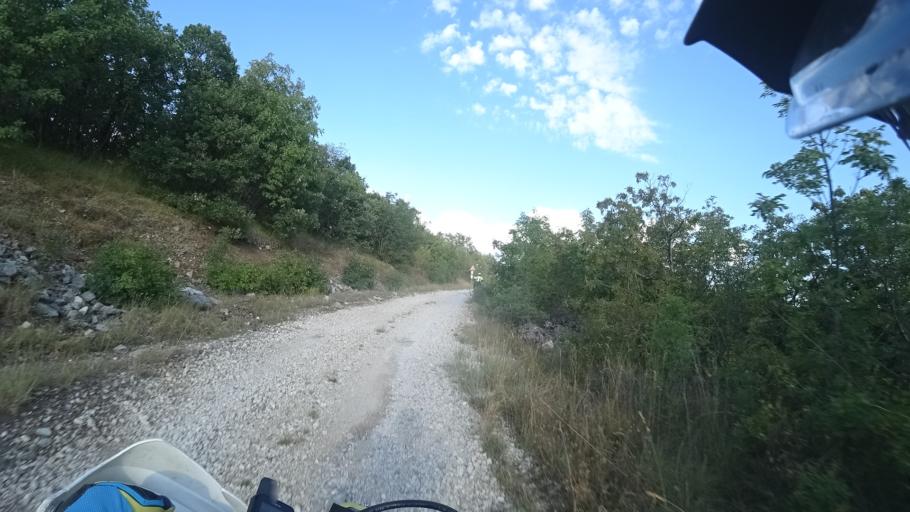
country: HR
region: Sibensko-Kniniska
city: Knin
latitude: 44.1374
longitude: 16.1125
